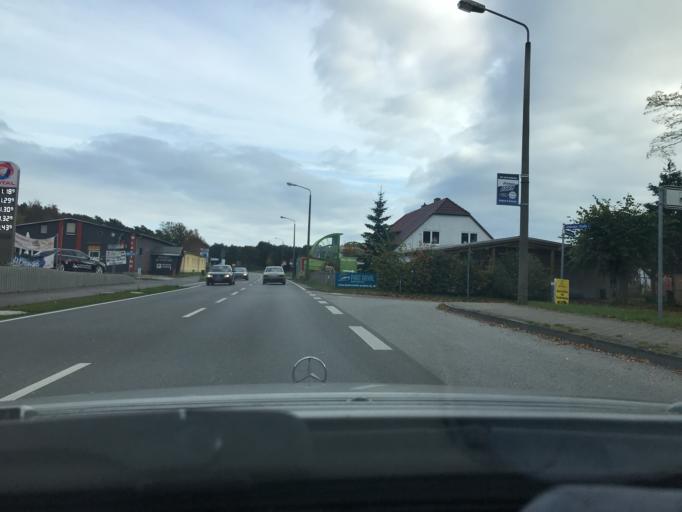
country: DE
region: Mecklenburg-Vorpommern
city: Ostseebad Zinnowitz
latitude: 54.0672
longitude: 13.9192
